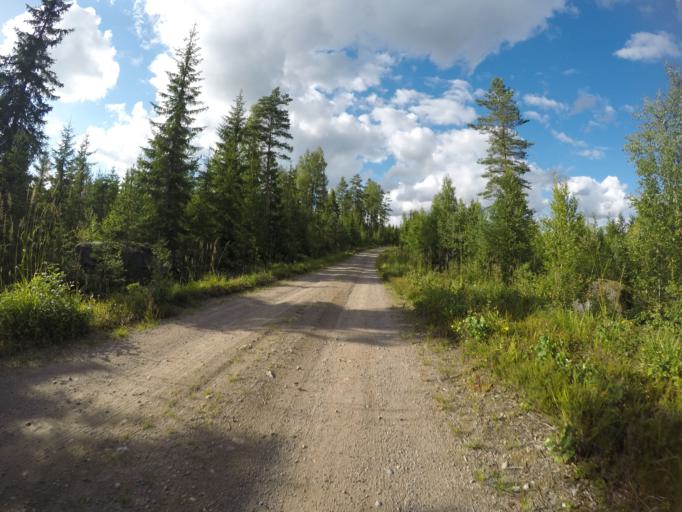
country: SE
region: OErebro
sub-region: Hallefors Kommun
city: Haellefors
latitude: 59.9503
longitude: 14.5629
